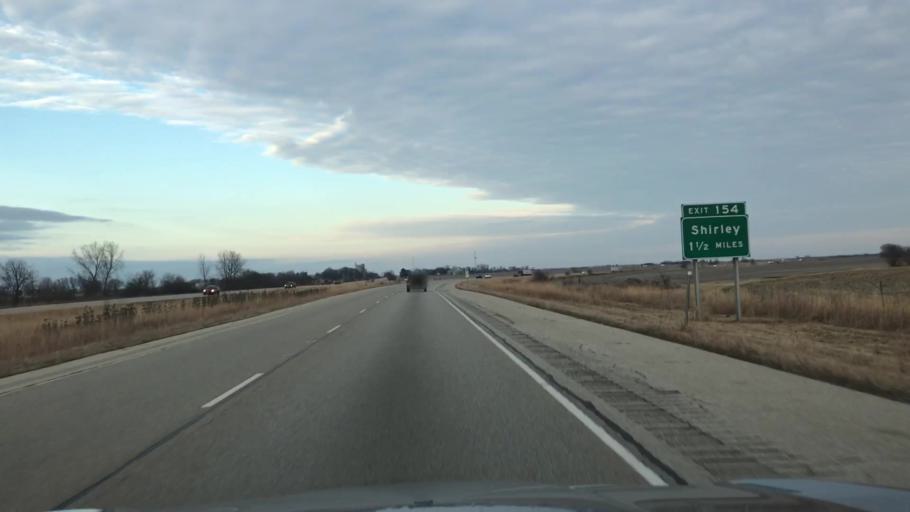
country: US
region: Illinois
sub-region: McLean County
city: Twin Grove
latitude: 40.3920
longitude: -89.0780
